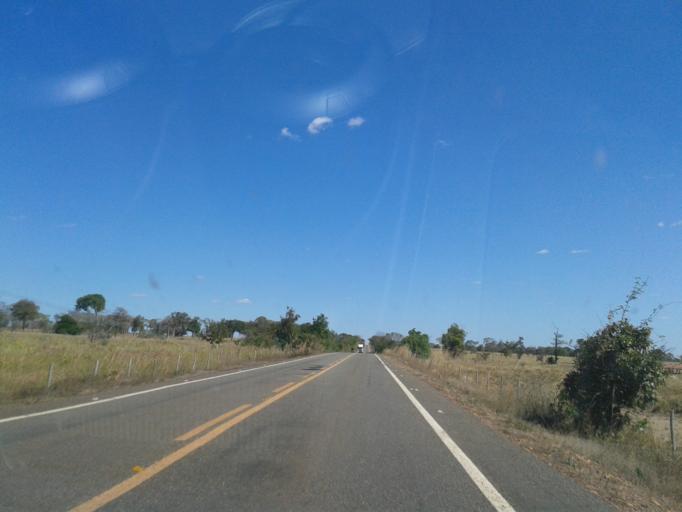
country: BR
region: Goias
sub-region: Sao Miguel Do Araguaia
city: Sao Miguel do Araguaia
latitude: -13.6545
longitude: -50.3213
